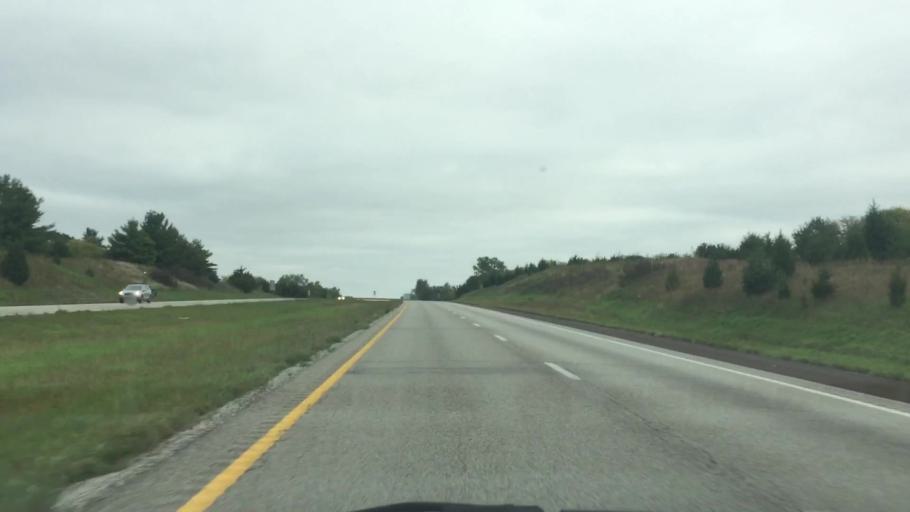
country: US
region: Missouri
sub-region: Clinton County
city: Cameron
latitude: 39.8899
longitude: -94.1566
